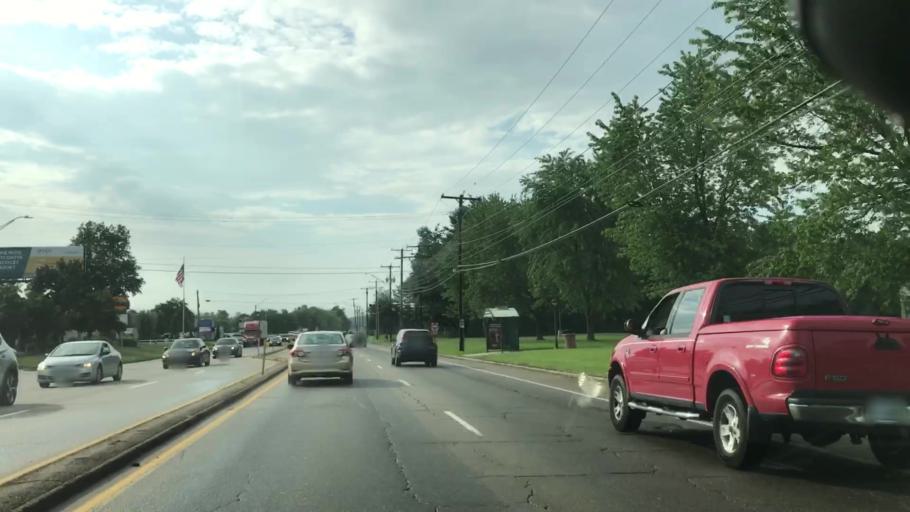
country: US
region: New Hampshire
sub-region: Hillsborough County
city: Nashua
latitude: 42.7937
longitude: -71.5243
